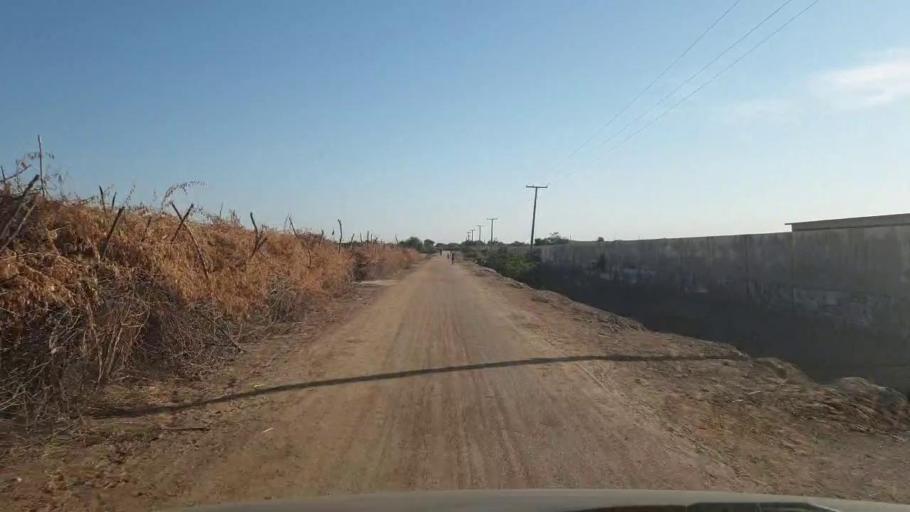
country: PK
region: Sindh
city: Dhoro Naro
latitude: 25.4273
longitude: 69.5438
